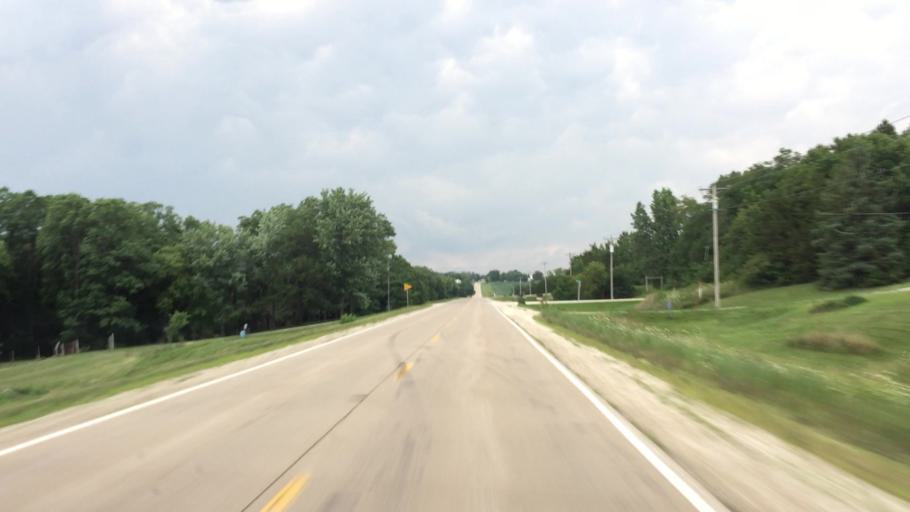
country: US
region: Iowa
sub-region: Lee County
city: Fort Madison
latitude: 40.7172
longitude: -91.3299
